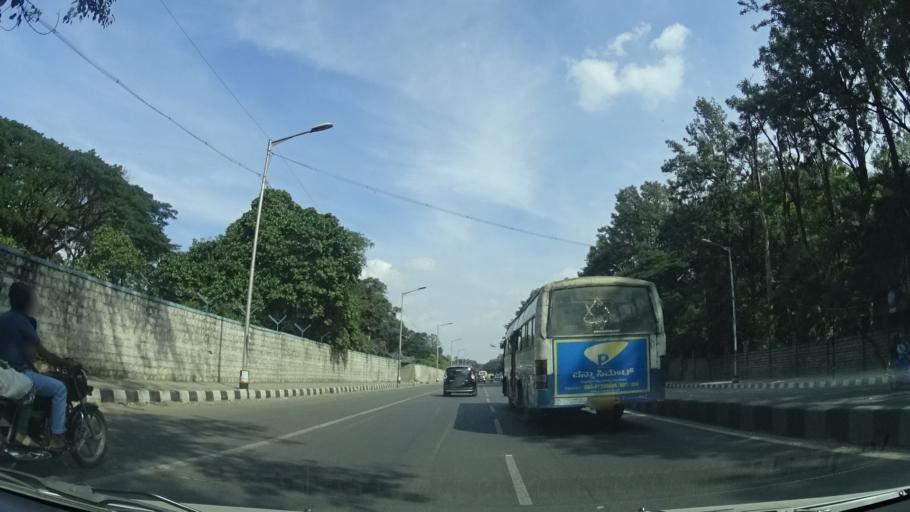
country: IN
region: Karnataka
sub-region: Bangalore Urban
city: Bangalore
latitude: 13.0150
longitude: 77.5799
